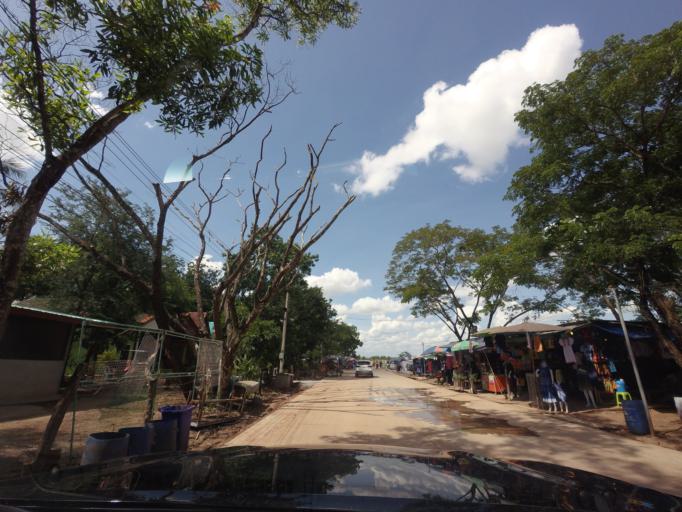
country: TH
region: Changwat Udon Thani
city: Ban Dung
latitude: 17.7438
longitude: 103.3584
